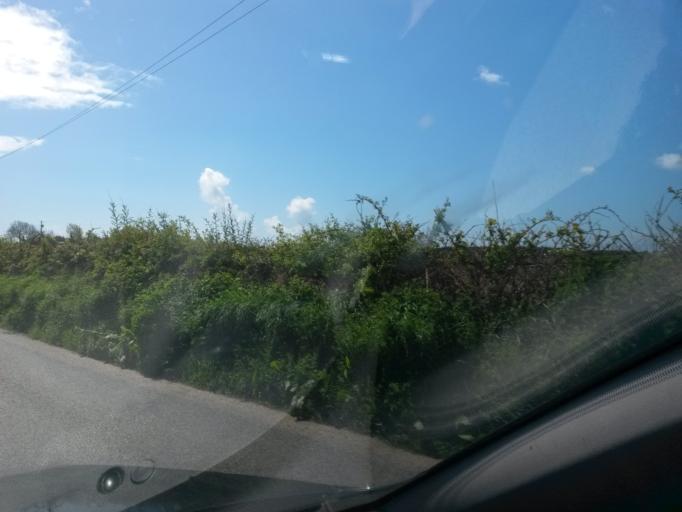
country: IE
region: Munster
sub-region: Waterford
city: Dunmore East
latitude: 52.2424
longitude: -6.8586
